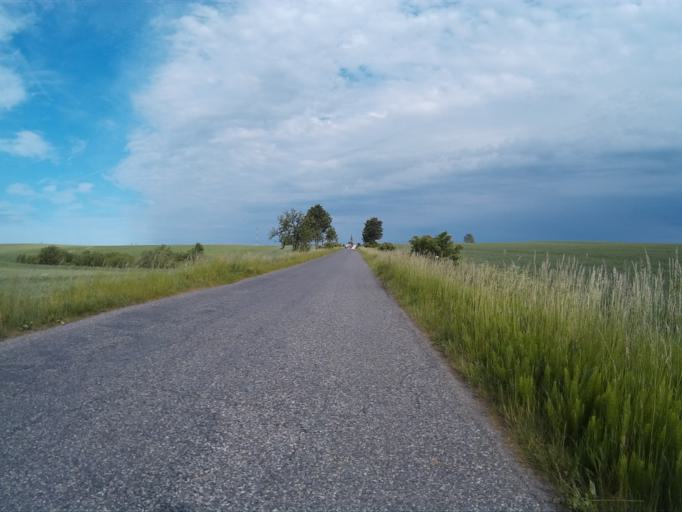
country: PL
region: Kujawsko-Pomorskie
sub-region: Powiat tucholski
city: Lubiewo
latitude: 53.4676
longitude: 18.0087
